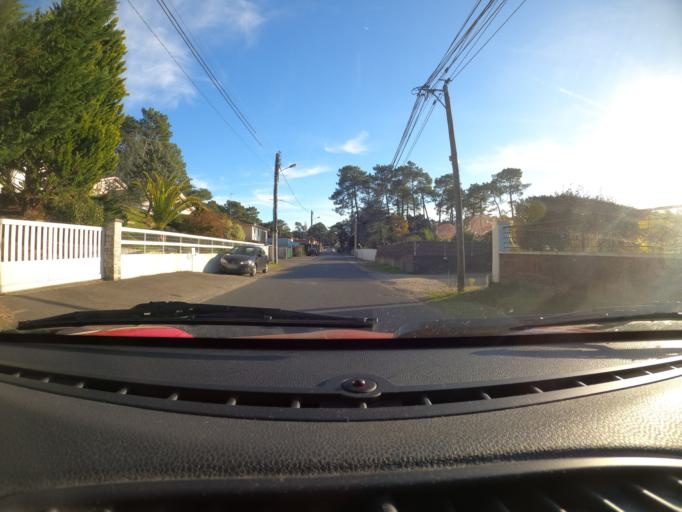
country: FR
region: Aquitaine
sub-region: Departement des Landes
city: Ondres
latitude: 43.5687
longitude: -1.4466
